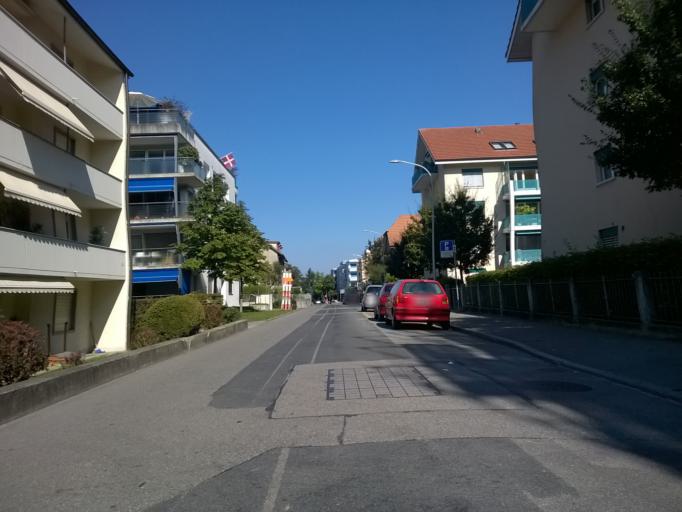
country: CH
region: Bern
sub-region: Bern-Mittelland District
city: Koniz
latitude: 46.9433
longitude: 7.3988
